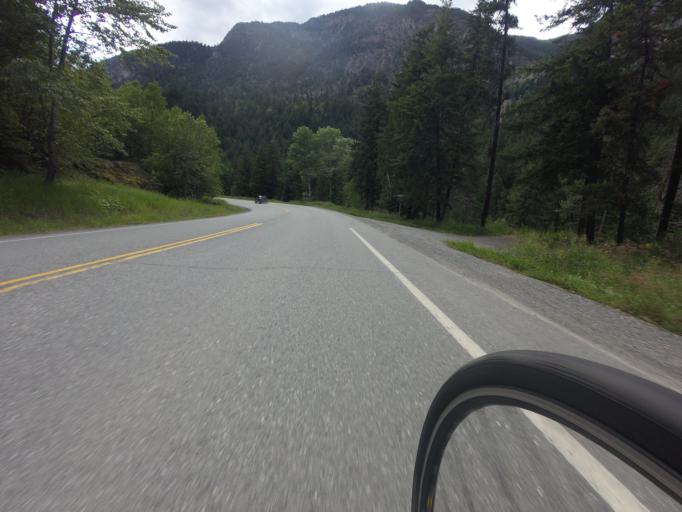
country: CA
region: British Columbia
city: Lillooet
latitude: 50.6386
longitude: -122.0872
